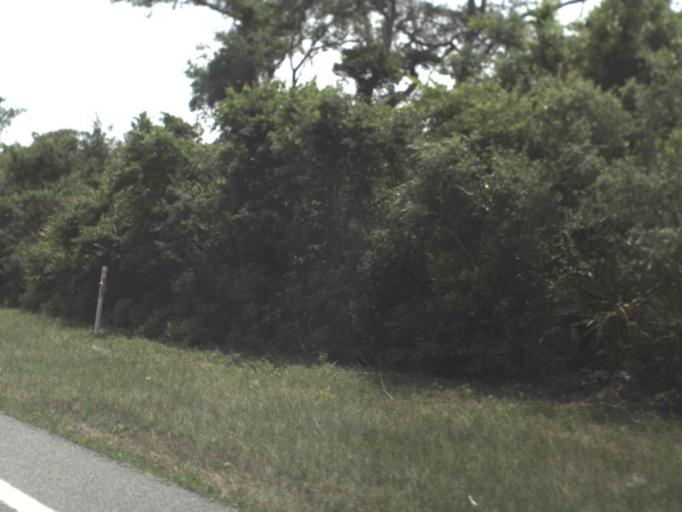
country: US
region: Florida
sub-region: Duval County
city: Atlantic Beach
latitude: 30.4958
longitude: -81.4456
